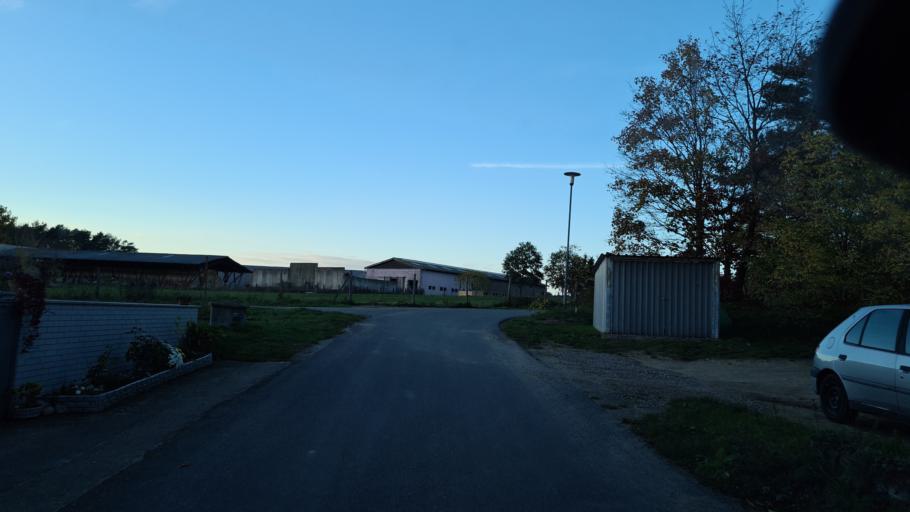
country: DE
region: Saxony
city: Belgern
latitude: 51.4453
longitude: 13.1113
